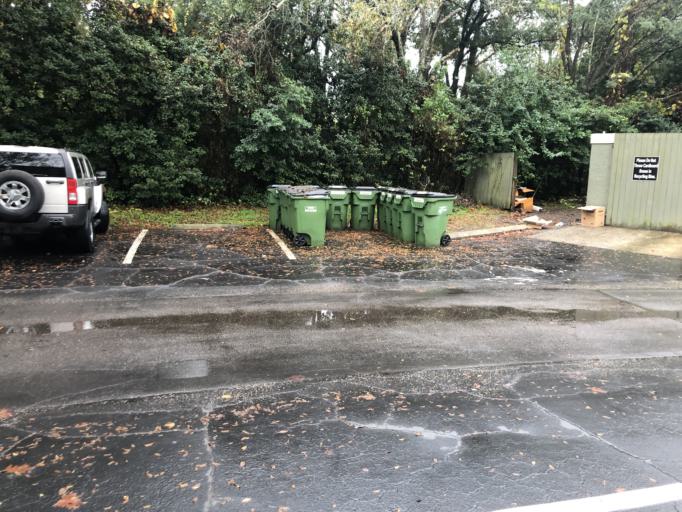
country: US
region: Florida
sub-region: Seminole County
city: Altamonte Springs
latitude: 28.6677
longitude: -81.3987
